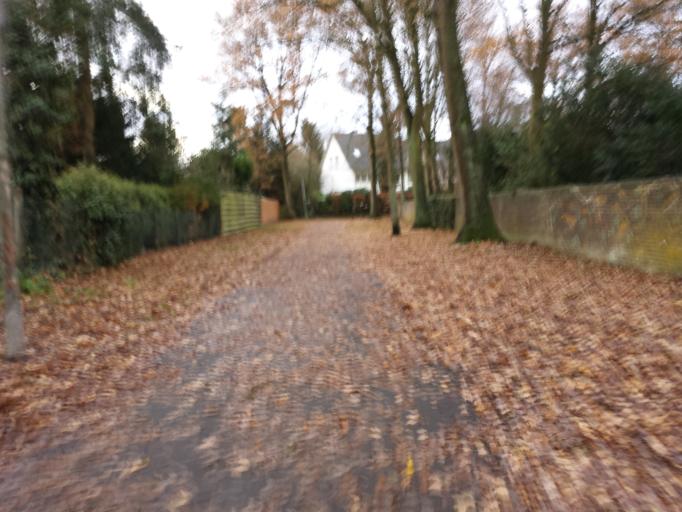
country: DE
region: Bremen
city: Bremen
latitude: 53.0959
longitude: 8.8609
